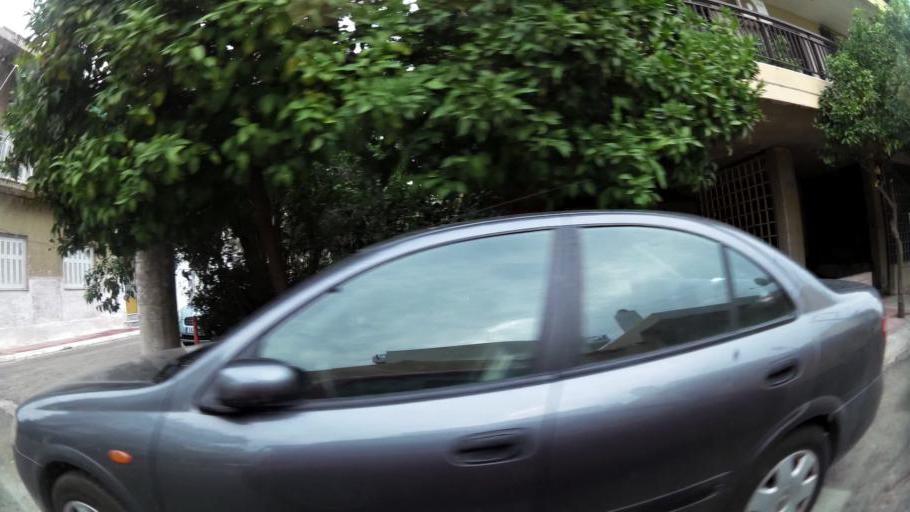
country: GR
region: Attica
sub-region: Nomarchia Athinas
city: Agioi Anargyroi
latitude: 38.0206
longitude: 23.7172
